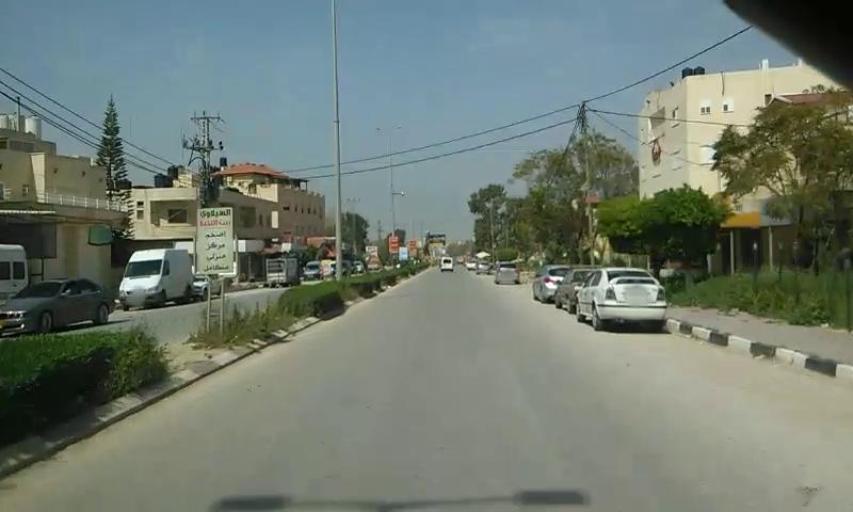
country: PS
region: West Bank
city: Janin
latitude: 32.4688
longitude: 35.3045
